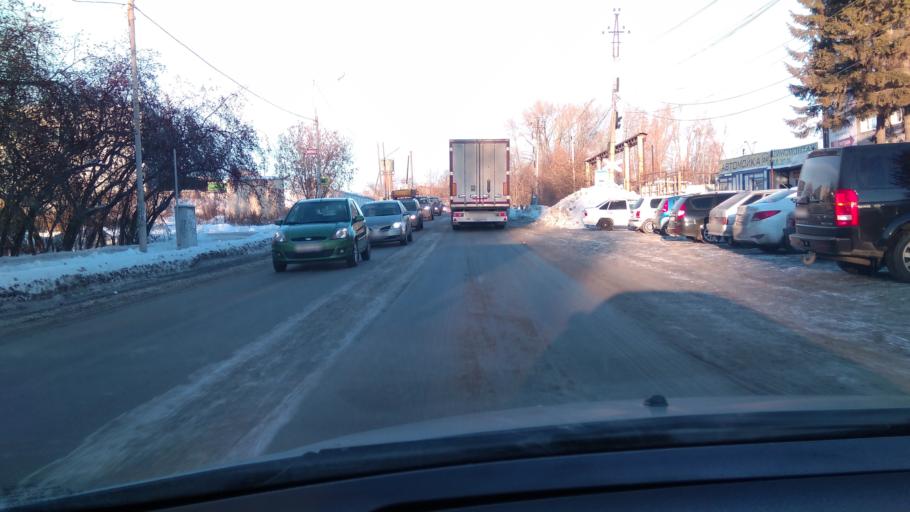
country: RU
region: Sverdlovsk
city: Sovkhoznyy
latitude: 56.7559
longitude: 60.6256
